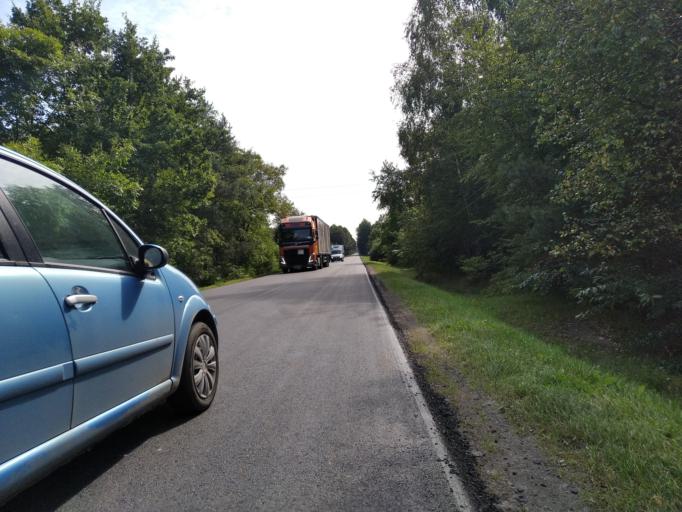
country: PL
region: Subcarpathian Voivodeship
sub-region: Powiat ropczycko-sedziszowski
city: Ostrow
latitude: 50.1549
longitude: 21.5598
